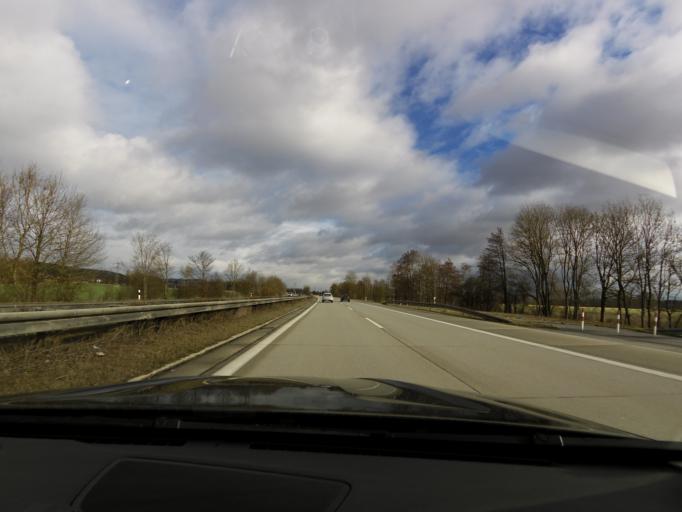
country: DE
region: Bavaria
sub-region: Lower Bavaria
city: Eching
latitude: 48.5169
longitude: 12.0600
